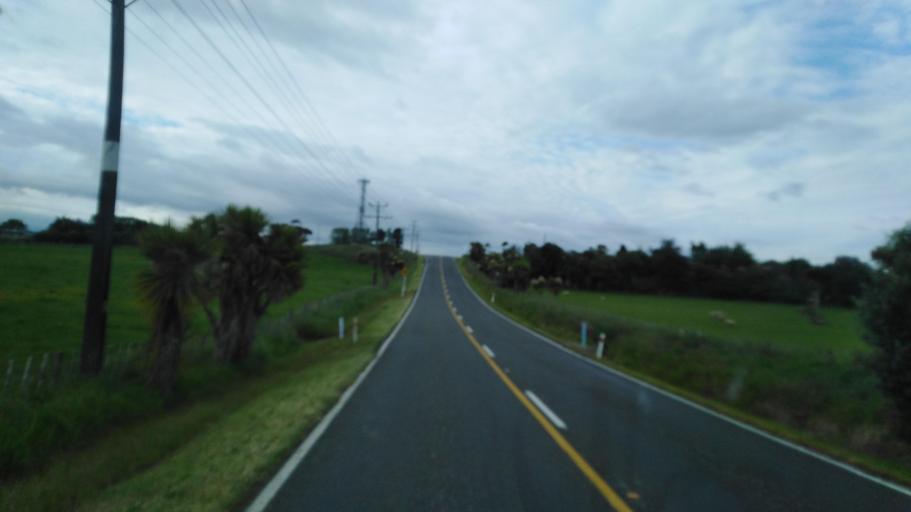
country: NZ
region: Manawatu-Wanganui
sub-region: Rangitikei District
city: Bulls
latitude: -40.1083
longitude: 175.3596
